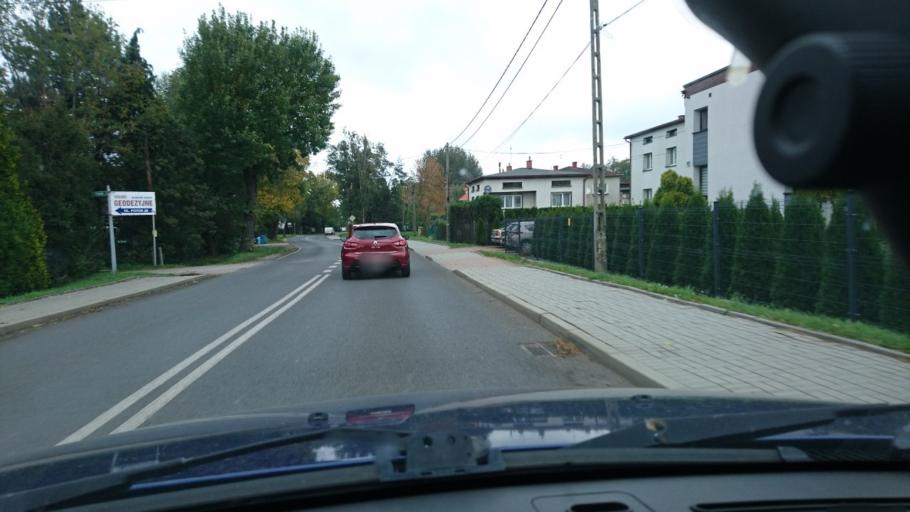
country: PL
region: Silesian Voivodeship
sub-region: Powiat bielski
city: Jaworze
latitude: 49.8049
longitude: 18.9820
